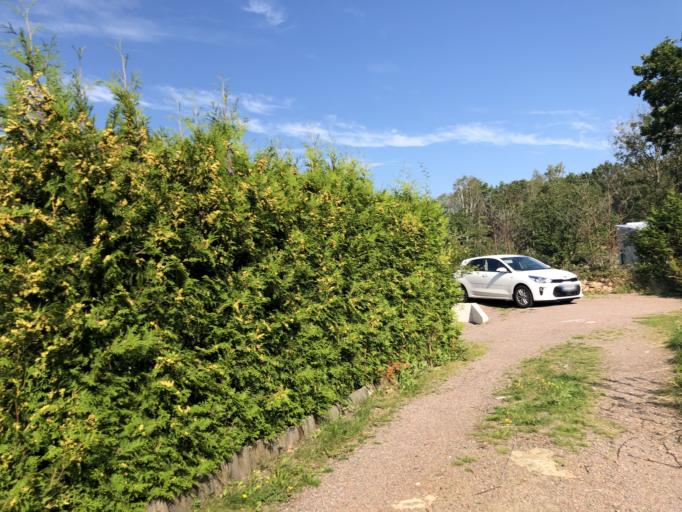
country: SE
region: Vaestra Goetaland
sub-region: Goteborg
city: Goeteborg
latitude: 57.7395
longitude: 11.9630
